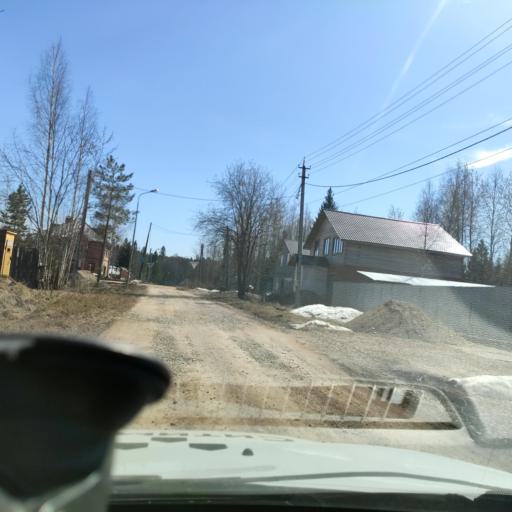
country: RU
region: Perm
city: Ferma
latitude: 57.9282
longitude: 56.4211
